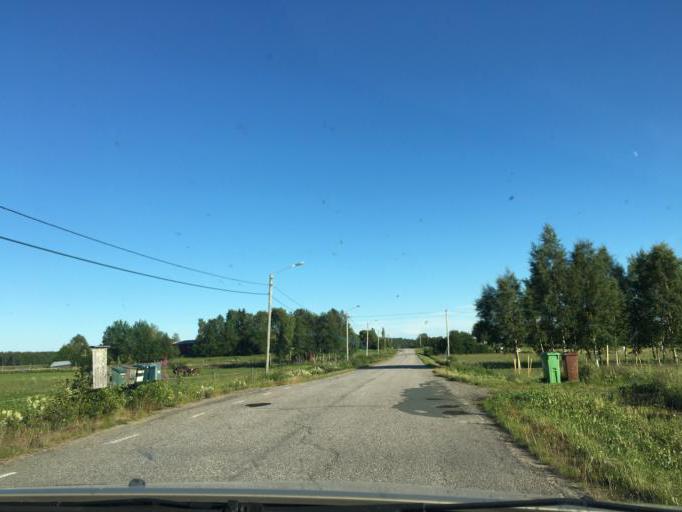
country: SE
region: Norrbotten
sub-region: Kalix Kommun
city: Rolfs
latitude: 65.8962
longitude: 22.9397
